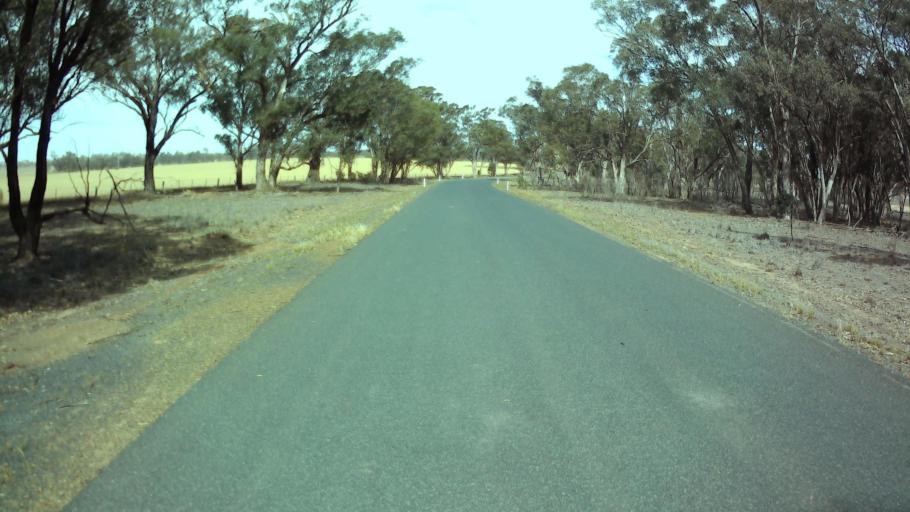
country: AU
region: New South Wales
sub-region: Weddin
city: Grenfell
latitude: -33.8087
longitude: 148.0680
